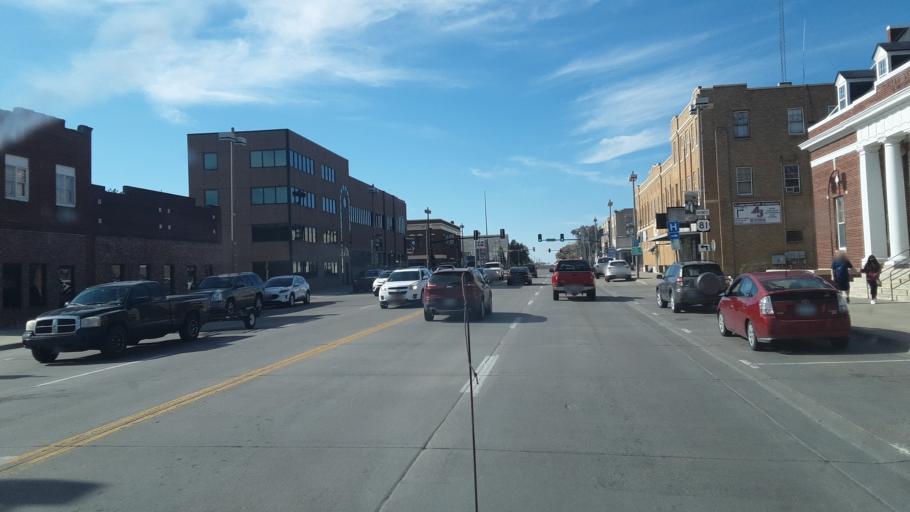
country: US
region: Kansas
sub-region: McPherson County
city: McPherson
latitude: 38.3694
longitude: -97.6656
